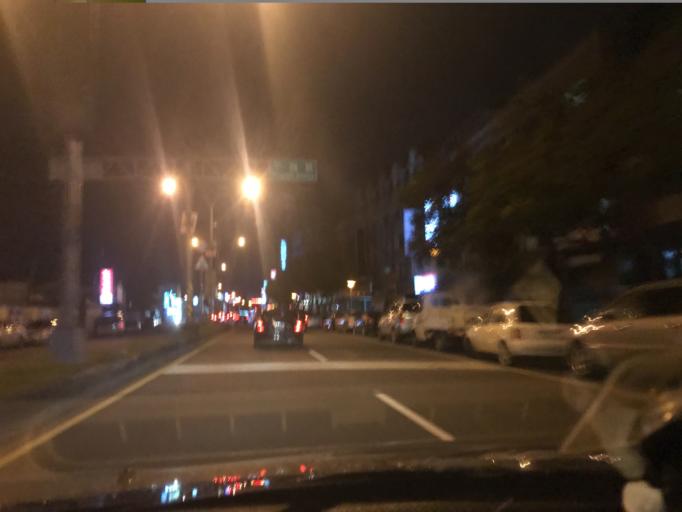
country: TW
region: Taiwan
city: Daxi
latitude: 24.9415
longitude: 121.2248
